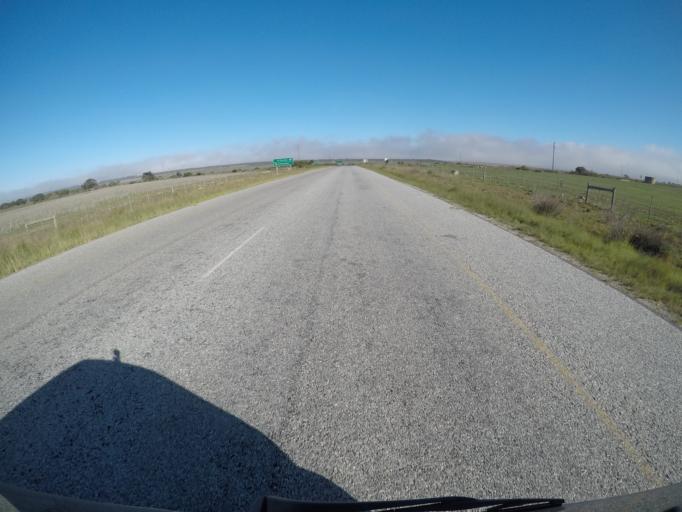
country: ZA
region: Western Cape
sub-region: Eden District Municipality
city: Mossel Bay
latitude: -34.1790
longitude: 22.0169
